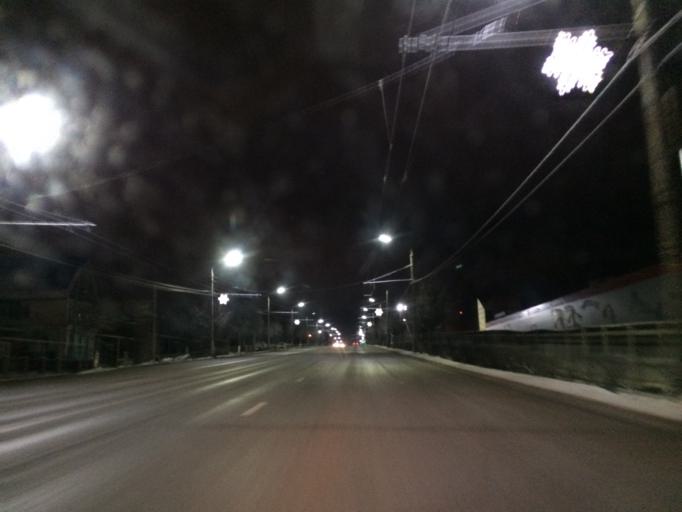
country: RU
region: Tula
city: Gorelki
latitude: 54.2315
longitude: 37.6256
